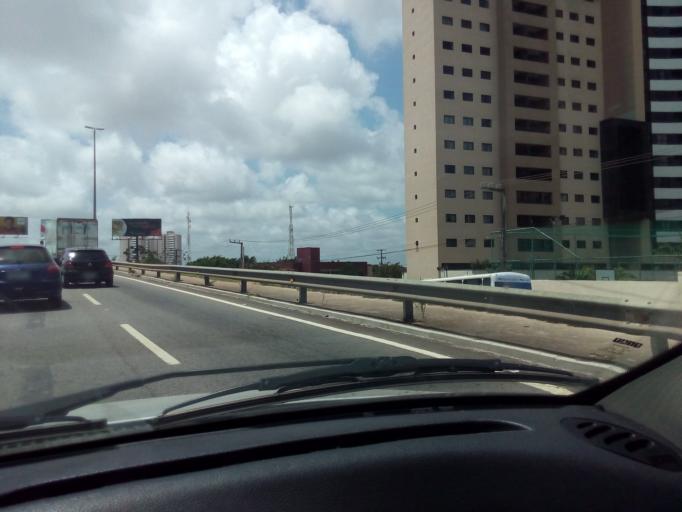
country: BR
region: Rio Grande do Norte
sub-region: Natal
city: Natal
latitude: -5.8471
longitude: -35.2090
